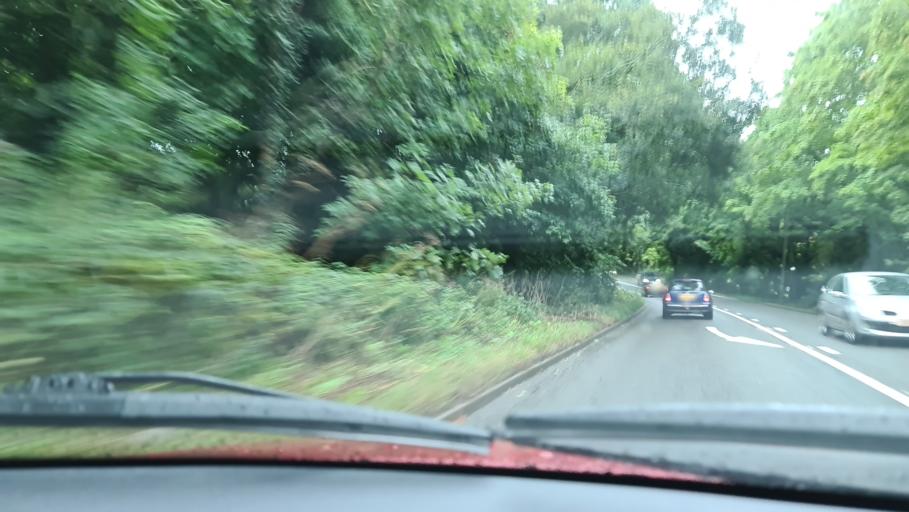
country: GB
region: England
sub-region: Buckinghamshire
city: Beaconsfield
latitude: 51.6137
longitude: -0.6327
